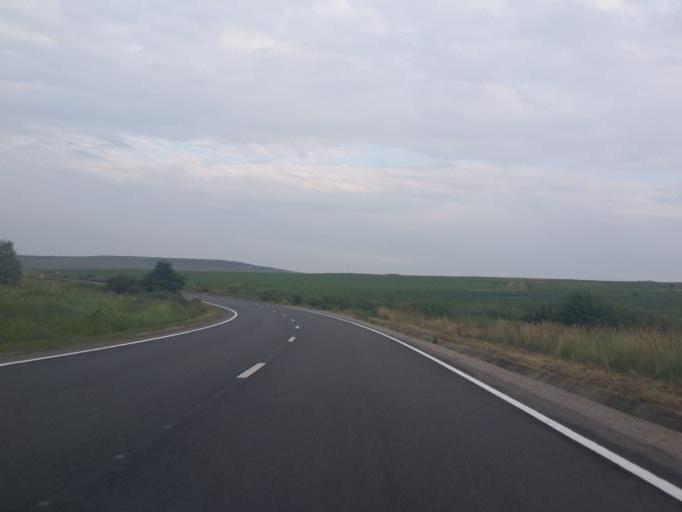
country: RO
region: Cluj
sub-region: Comuna Sanpaul
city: Sanpaul
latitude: 46.9227
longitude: 23.4099
